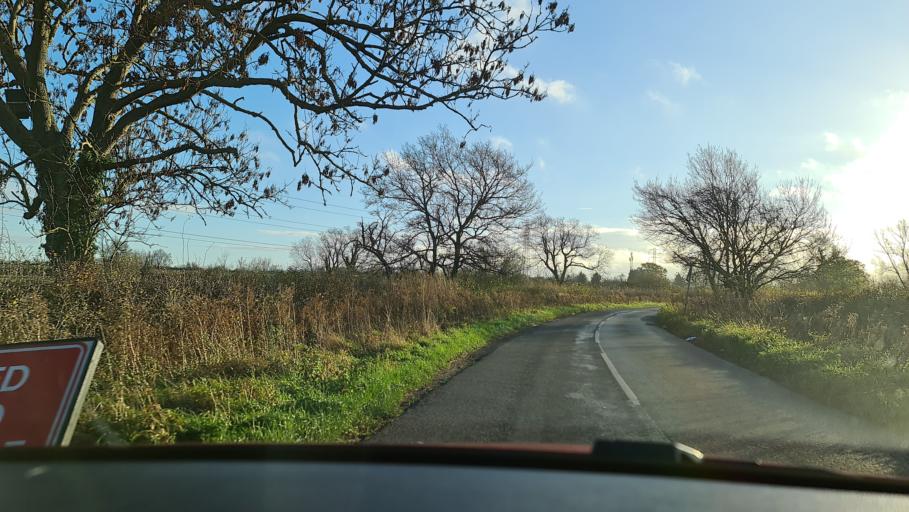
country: GB
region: England
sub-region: Buckinghamshire
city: Aylesbury
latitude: 51.7780
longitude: -0.8070
